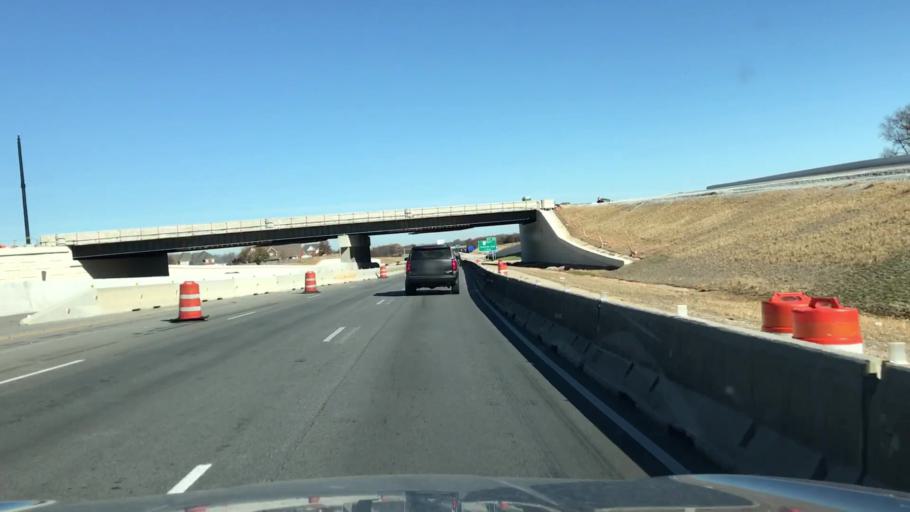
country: US
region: Arkansas
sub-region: Benton County
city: Bentonville
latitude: 36.3628
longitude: -94.1763
